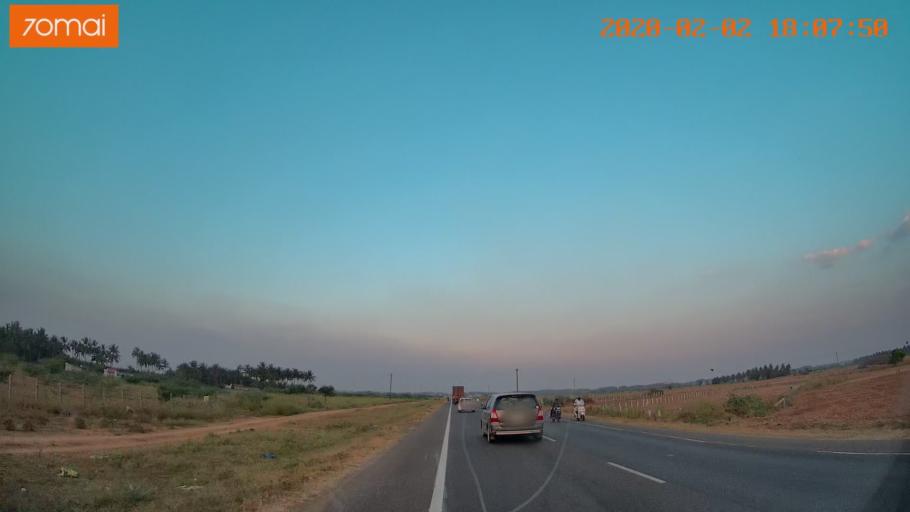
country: IN
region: Tamil Nadu
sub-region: Coimbatore
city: Chettipalaiyam
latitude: 10.9507
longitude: 77.0174
